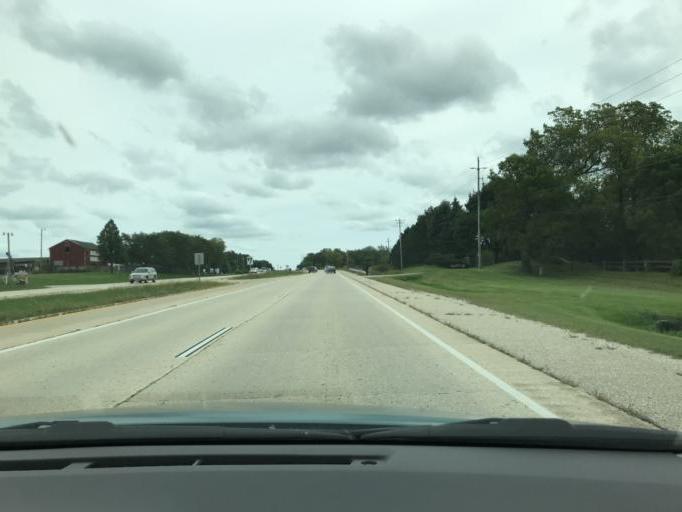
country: US
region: Wisconsin
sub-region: Kenosha County
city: Bristol
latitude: 42.5679
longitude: -88.0665
